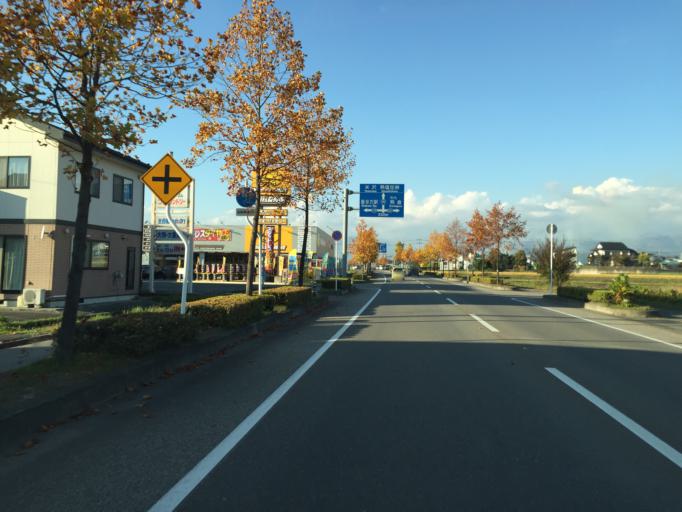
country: JP
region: Fukushima
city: Kitakata
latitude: 37.6461
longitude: 139.8886
